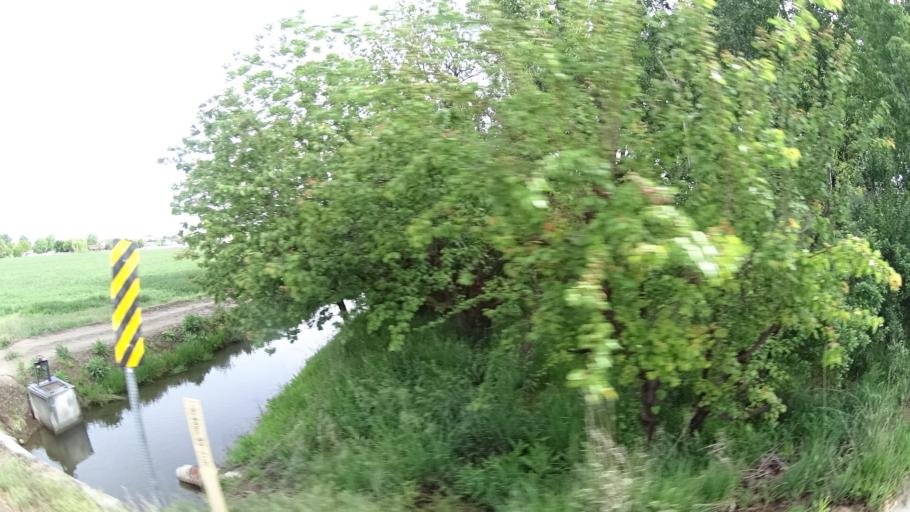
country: US
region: Idaho
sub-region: Ada County
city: Eagle
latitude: 43.7209
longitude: -116.4055
